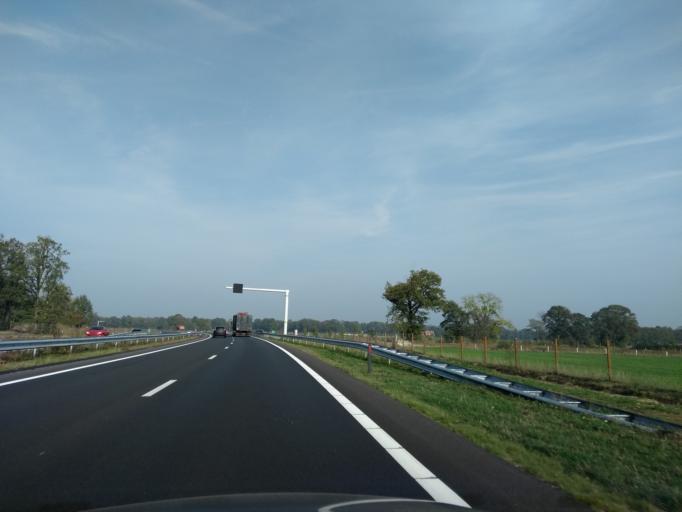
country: NL
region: Overijssel
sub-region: Gemeente Hengelo
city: Hengelo
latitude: 52.1917
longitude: 6.8182
